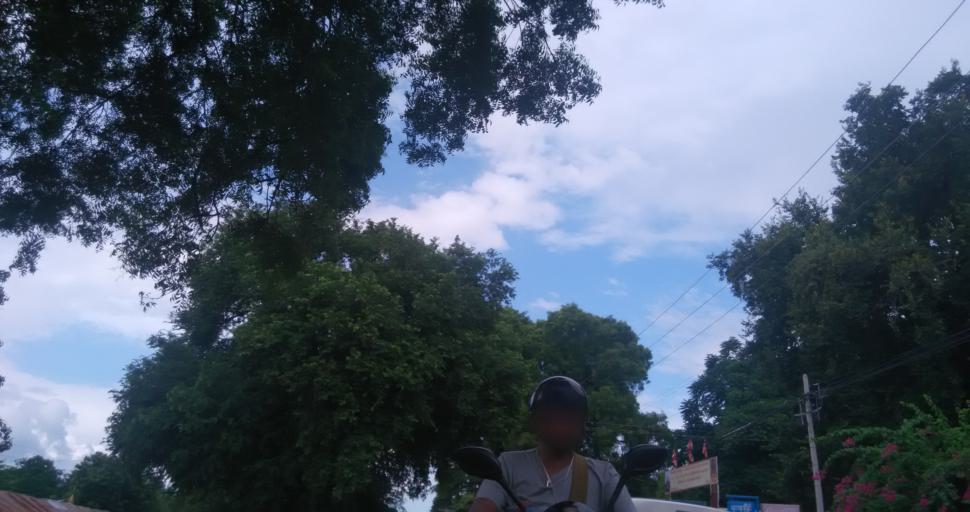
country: MM
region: Magway
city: Chauk
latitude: 21.1531
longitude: 94.8598
